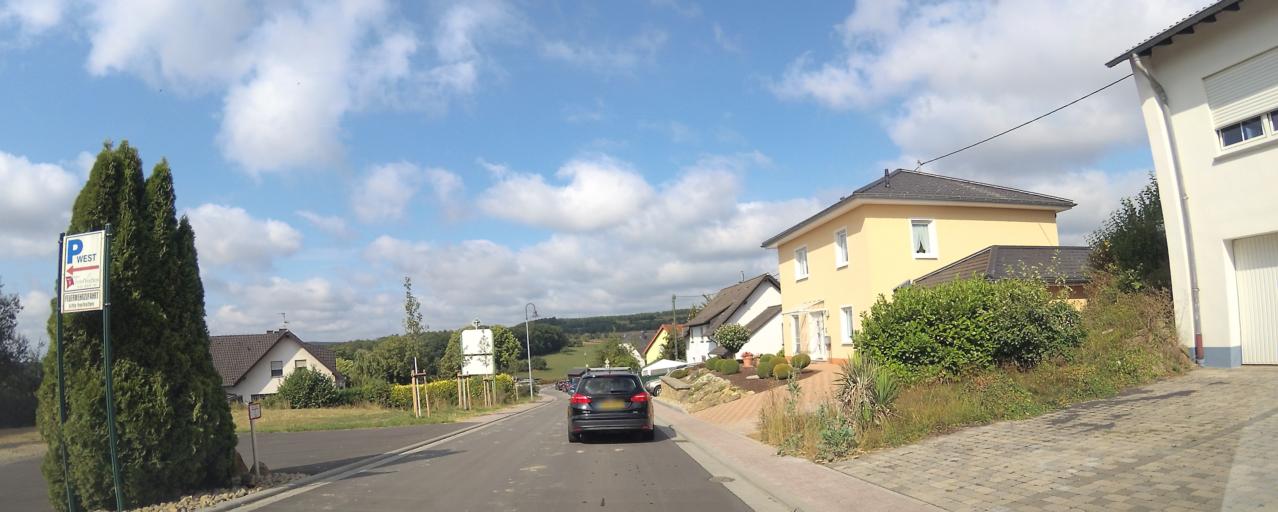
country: DE
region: Rheinland-Pfalz
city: Gondorf
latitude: 49.9656
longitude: 6.6234
